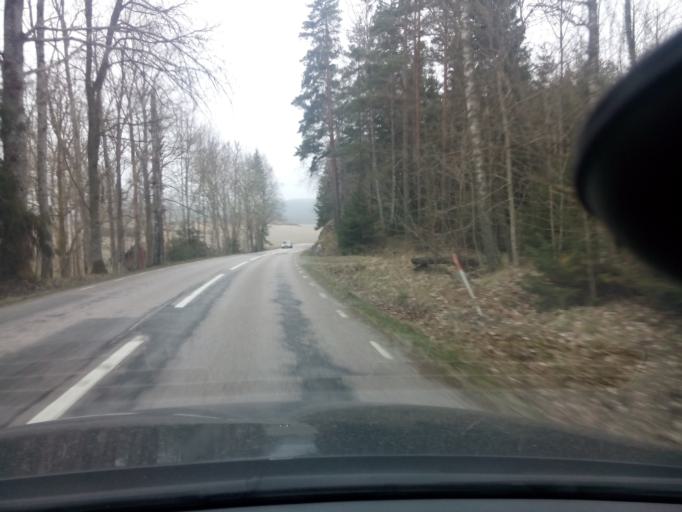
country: SE
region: Soedermanland
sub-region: Gnesta Kommun
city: Gnesta
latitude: 58.9686
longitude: 17.1451
